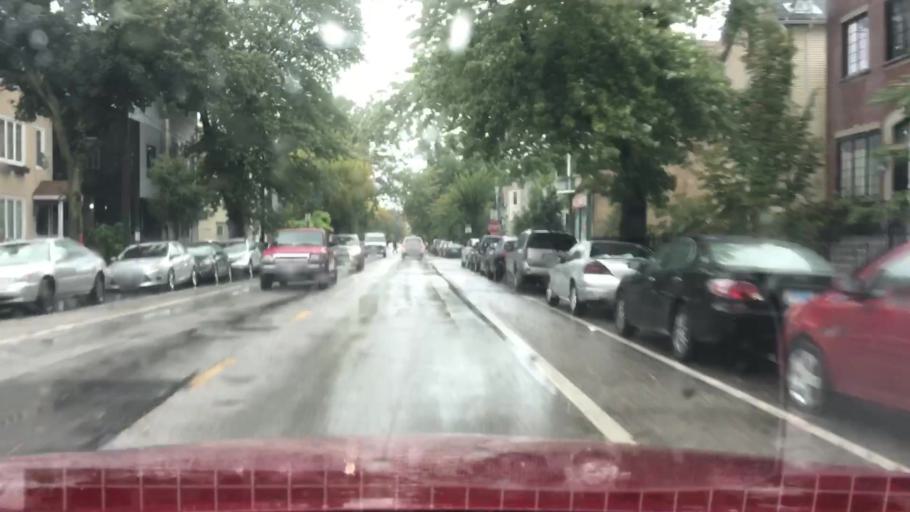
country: US
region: Illinois
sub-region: Cook County
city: Chicago
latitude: 41.9373
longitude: -87.6637
